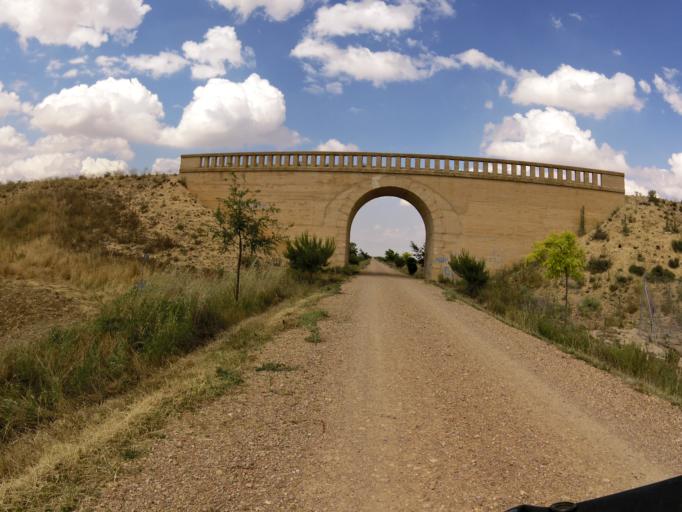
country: ES
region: Castille-La Mancha
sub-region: Provincia de Albacete
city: Albacete
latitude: 38.9310
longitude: -1.9935
